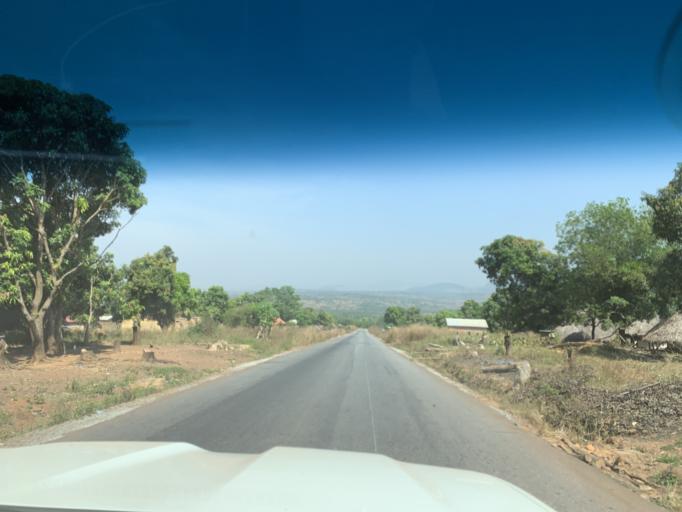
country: GN
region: Kindia
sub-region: Kindia
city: Kindia
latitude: 10.0815
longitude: -12.6440
